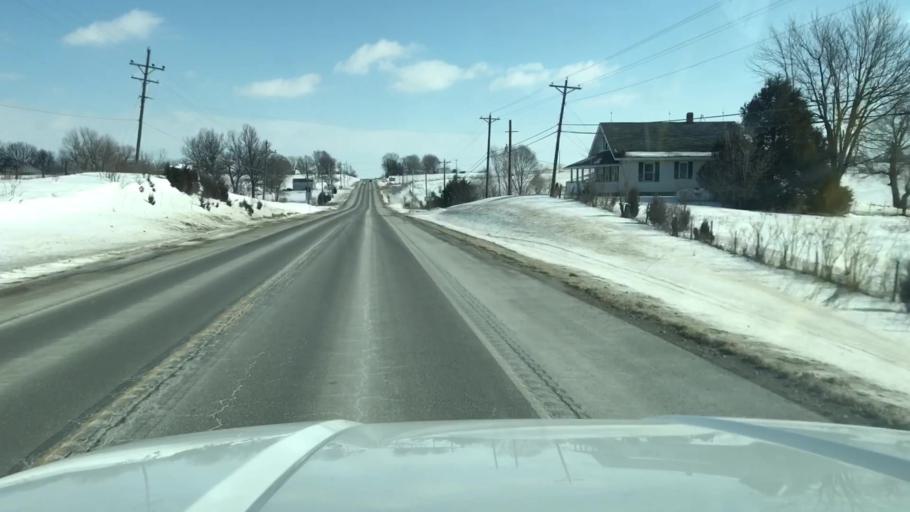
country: US
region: Missouri
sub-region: Nodaway County
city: Maryville
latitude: 40.3446
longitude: -94.8028
